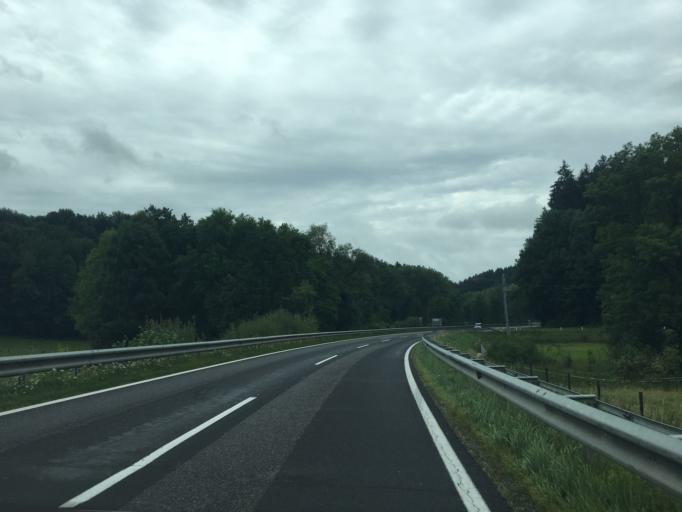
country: AT
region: Salzburg
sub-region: Politischer Bezirk Salzburg-Umgebung
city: Dorfbeuern
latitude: 48.1308
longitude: 13.0118
